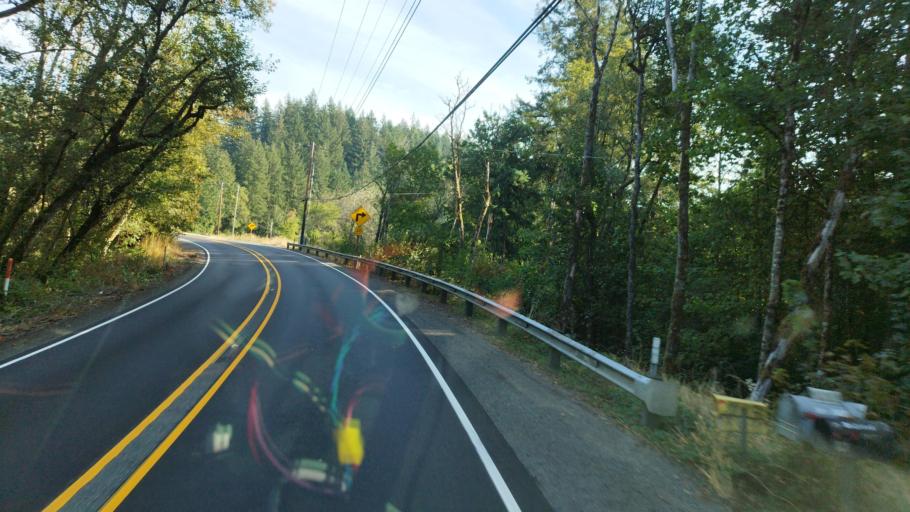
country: US
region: Oregon
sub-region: Washington County
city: Bethany
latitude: 45.6059
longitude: -122.8627
